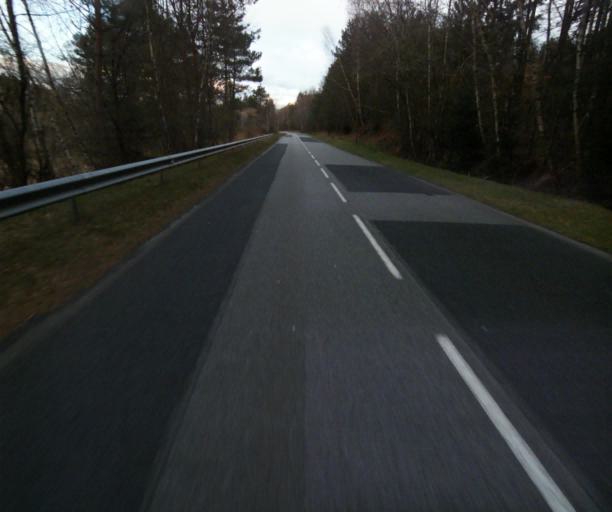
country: FR
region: Limousin
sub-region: Departement de la Correze
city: Correze
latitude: 45.2824
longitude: 1.9232
